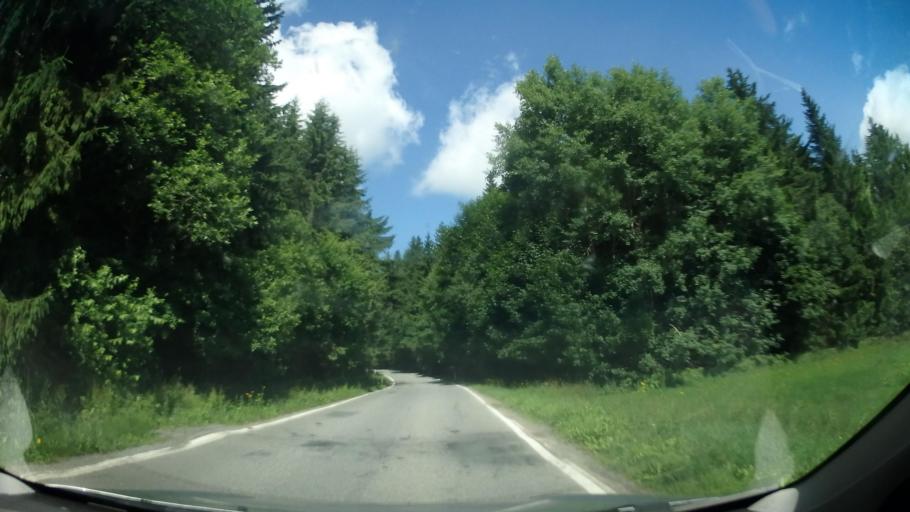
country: CZ
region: Vysocina
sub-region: Okres Zd'ar nad Sazavou
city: Nove Mesto na Morave
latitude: 49.6287
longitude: 16.0618
